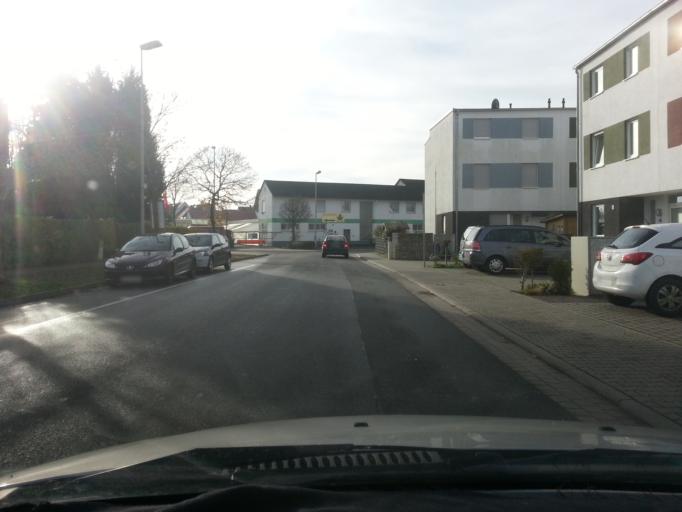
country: DE
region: Hesse
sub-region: Regierungsbezirk Darmstadt
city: Nauheim
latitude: 49.9480
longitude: 8.4564
